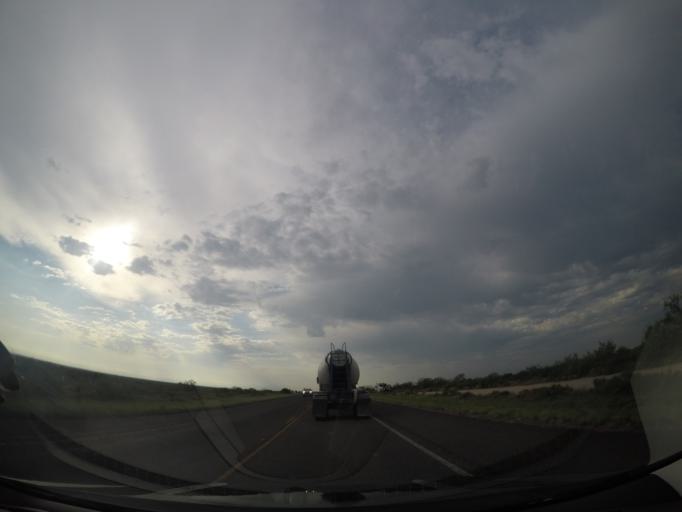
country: US
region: Texas
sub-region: Terrell County
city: Sanderson
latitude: 29.9485
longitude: -101.9908
